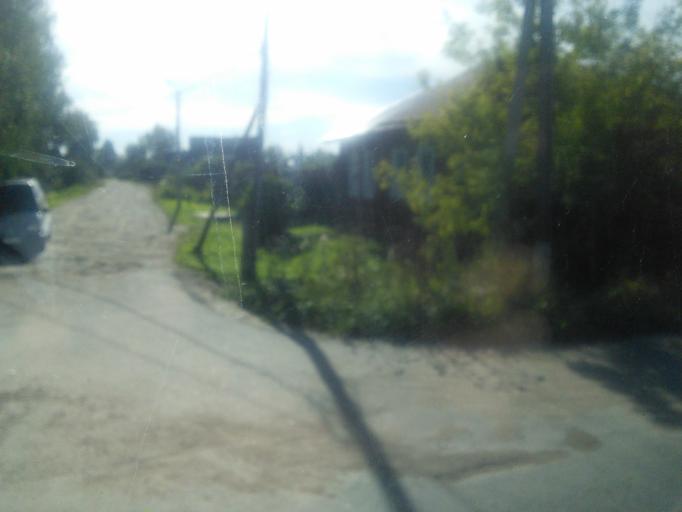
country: RU
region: Tverskaya
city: Bezhetsk
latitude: 57.7664
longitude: 36.7085
